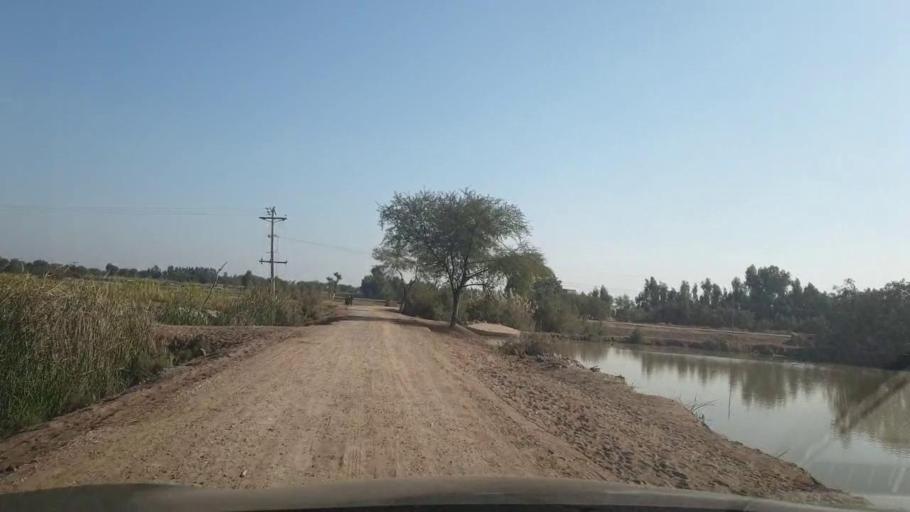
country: PK
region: Sindh
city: Khairpur
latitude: 28.1369
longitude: 69.6010
